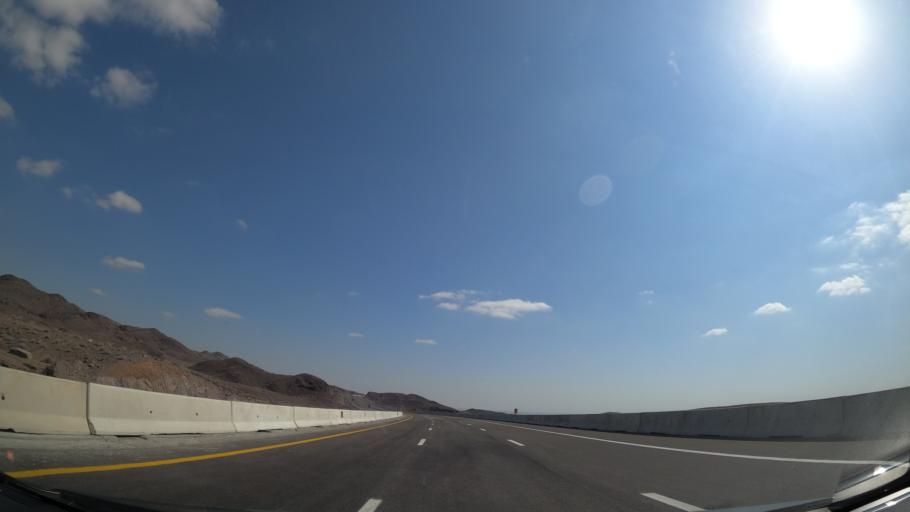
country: IR
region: Alborz
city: Eshtehard
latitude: 35.6647
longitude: 50.6493
